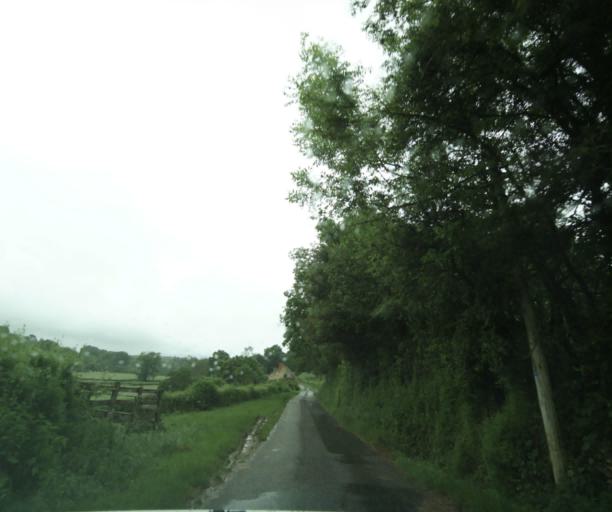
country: FR
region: Bourgogne
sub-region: Departement de Saone-et-Loire
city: Charolles
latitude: 46.4094
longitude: 4.3214
